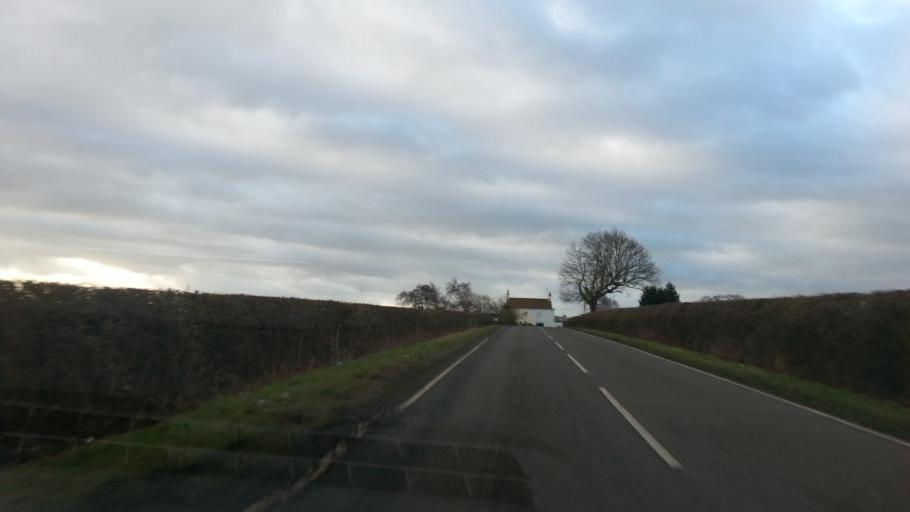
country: GB
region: England
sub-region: Nottinghamshire
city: Southwell
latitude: 53.1238
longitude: -0.8911
